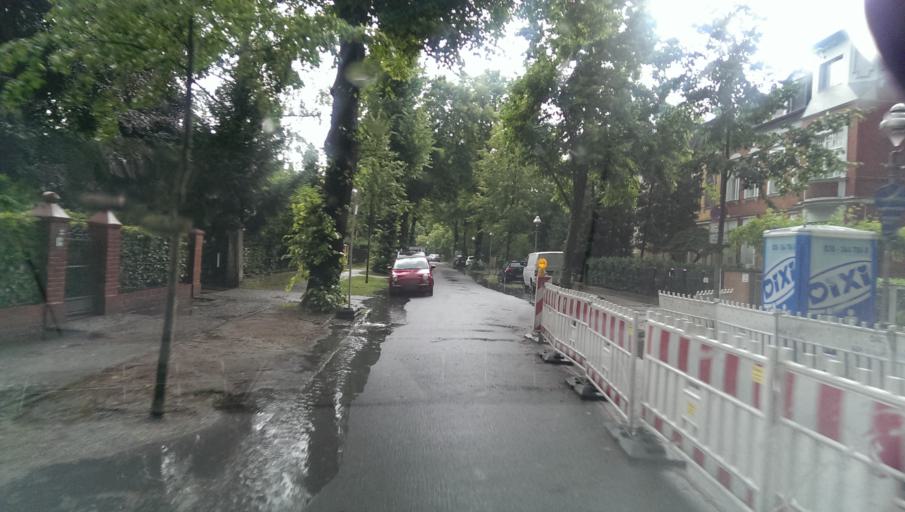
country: DE
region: Berlin
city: Lichterfelde
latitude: 52.4353
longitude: 13.2929
